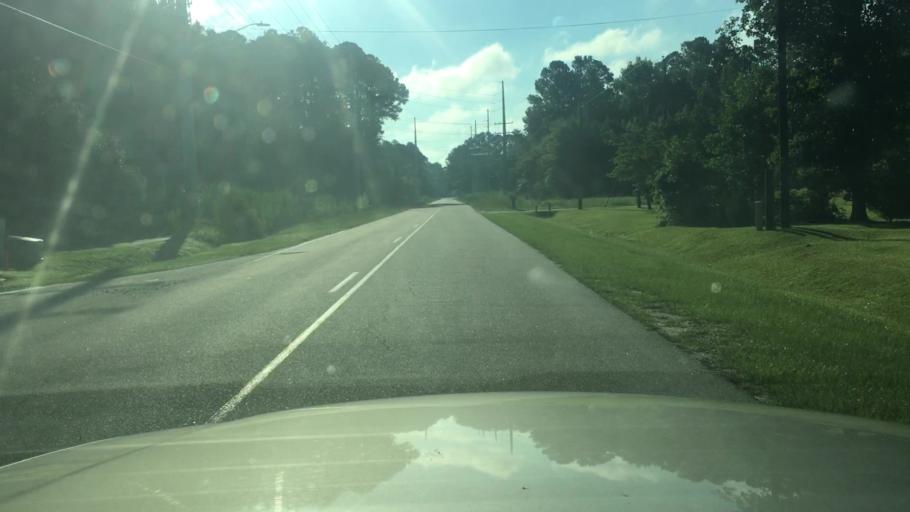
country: US
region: North Carolina
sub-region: Cumberland County
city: Eastover
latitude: 35.1498
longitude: -78.8664
